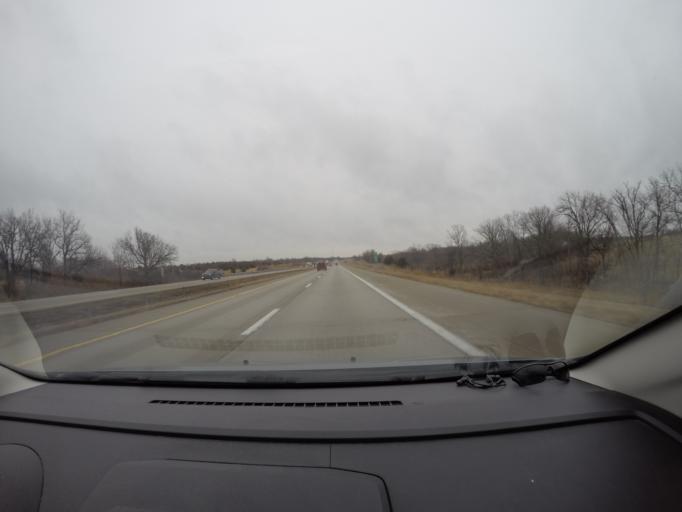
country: US
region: Missouri
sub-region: Montgomery County
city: Montgomery City
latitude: 38.9108
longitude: -91.6715
